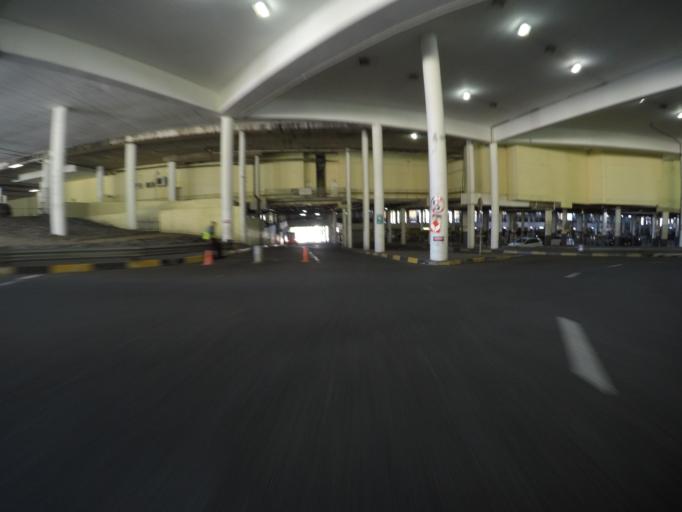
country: ZA
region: Eastern Cape
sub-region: Buffalo City Metropolitan Municipality
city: East London
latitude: -32.9702
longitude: 27.8997
